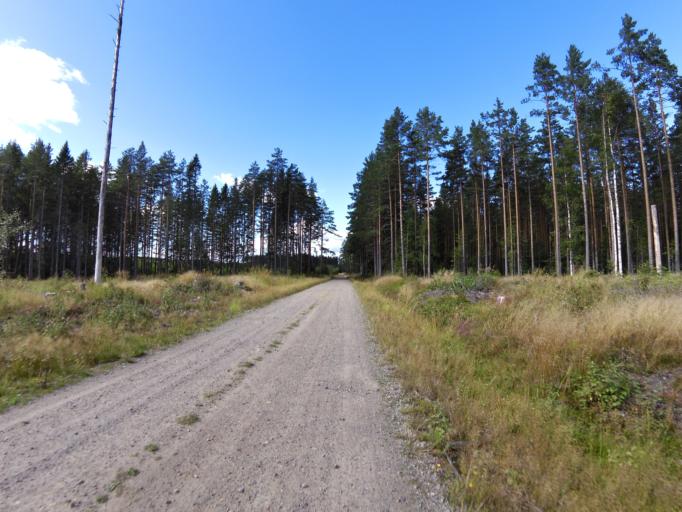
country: SE
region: Gaevleborg
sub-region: Ockelbo Kommun
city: Ockelbo
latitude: 60.8098
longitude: 16.7755
